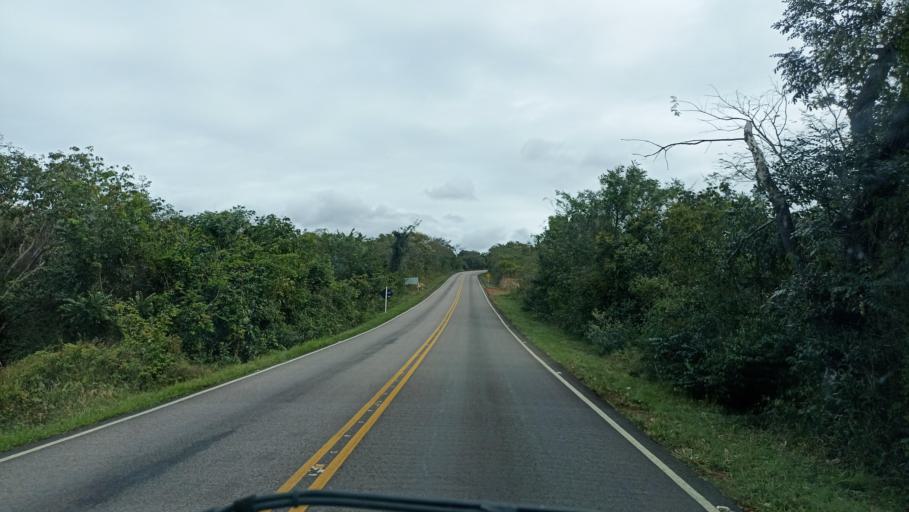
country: BR
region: Bahia
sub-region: Andarai
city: Vera Cruz
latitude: -12.9270
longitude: -41.2338
